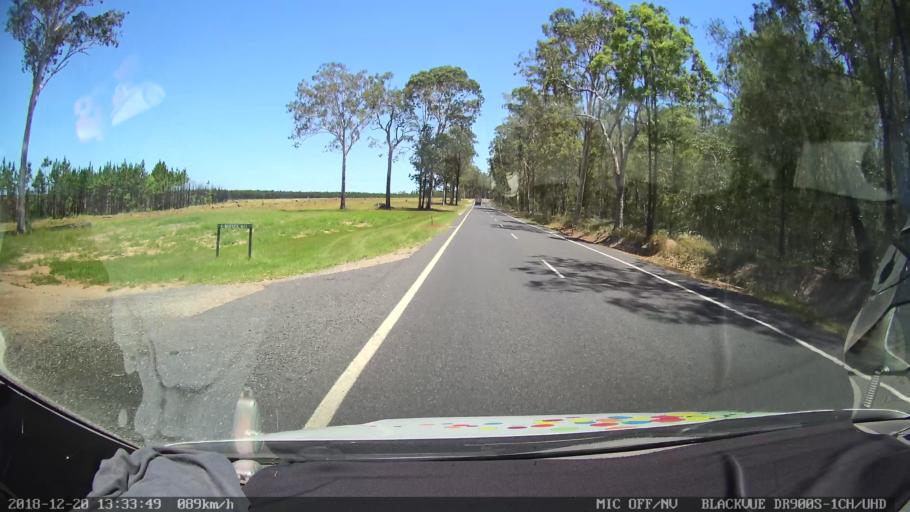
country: AU
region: New South Wales
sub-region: Clarence Valley
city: Gordon
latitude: -29.2505
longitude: 152.9852
